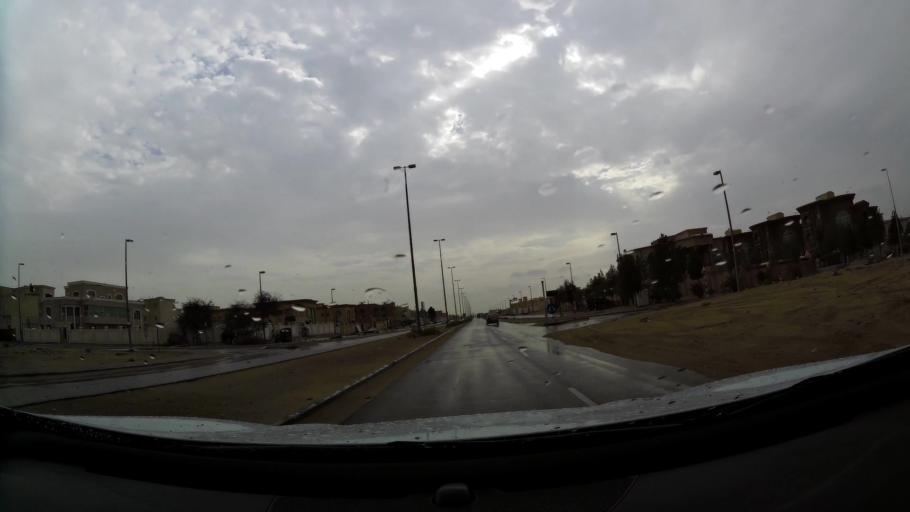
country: AE
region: Abu Dhabi
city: Abu Dhabi
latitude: 24.3608
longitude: 54.6314
